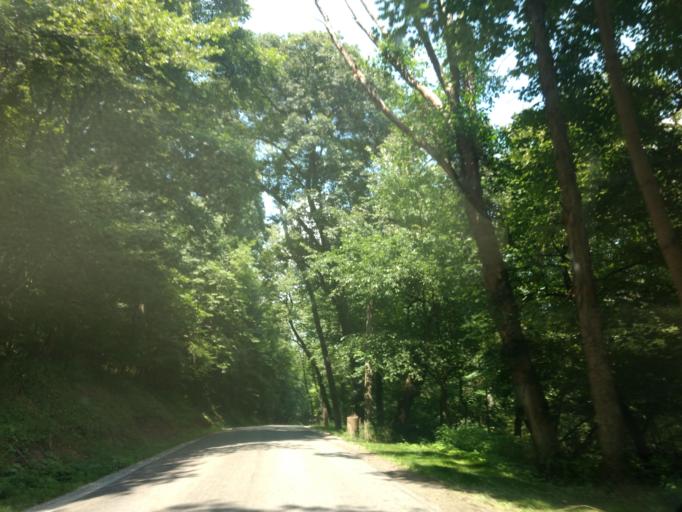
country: US
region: Pennsylvania
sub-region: Butler County
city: Evans City
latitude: 40.8306
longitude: -80.0745
